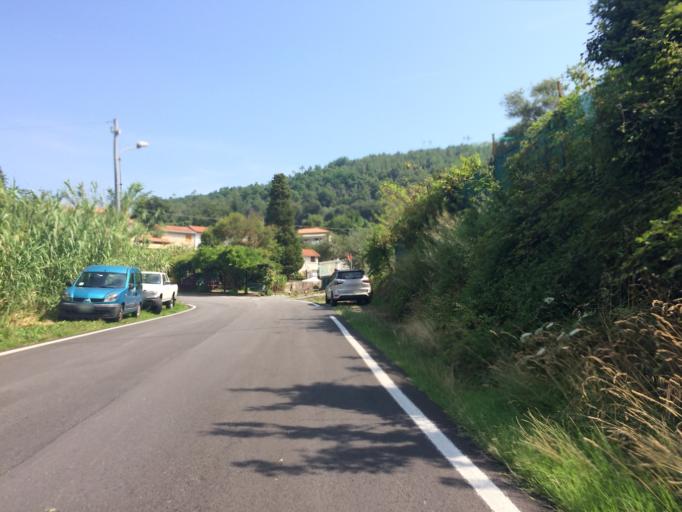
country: IT
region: Liguria
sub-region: Provincia di Savona
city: Varazze
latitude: 44.3818
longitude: 8.5688
